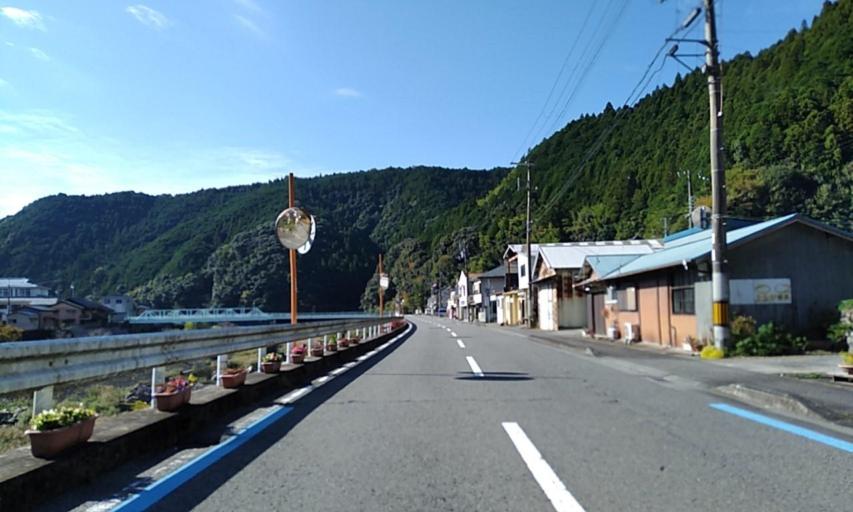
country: JP
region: Wakayama
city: Kainan
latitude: 34.0724
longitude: 135.3570
